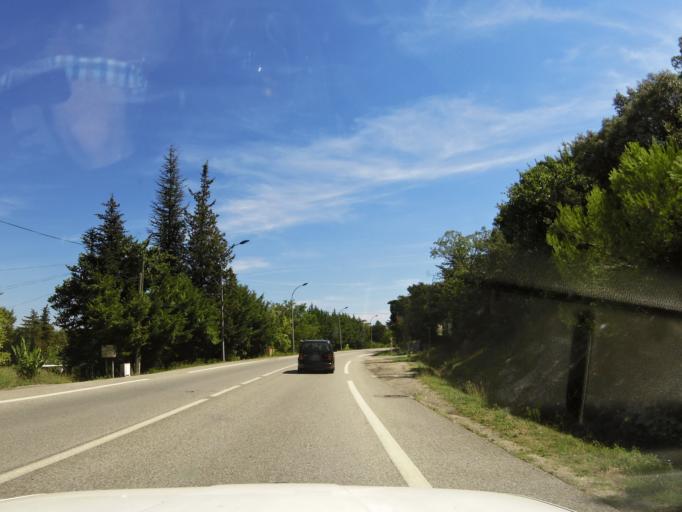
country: FR
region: Languedoc-Roussillon
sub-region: Departement du Gard
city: Bagnols-sur-Ceze
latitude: 44.1680
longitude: 4.6073
